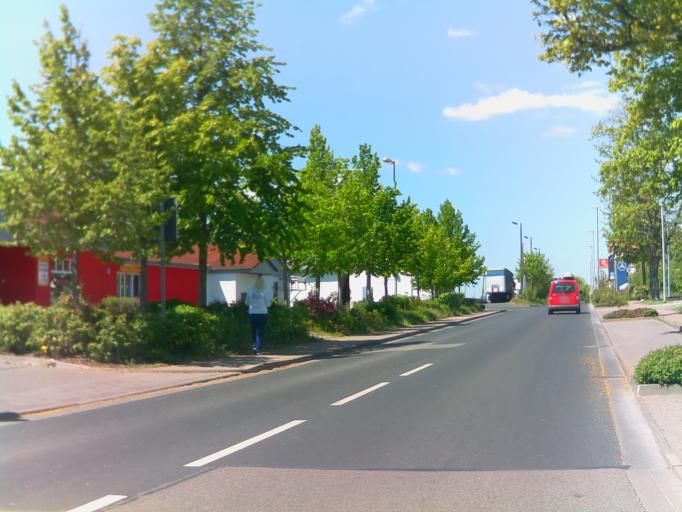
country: DE
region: Thuringia
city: Arnstadt
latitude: 50.8413
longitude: 10.9504
